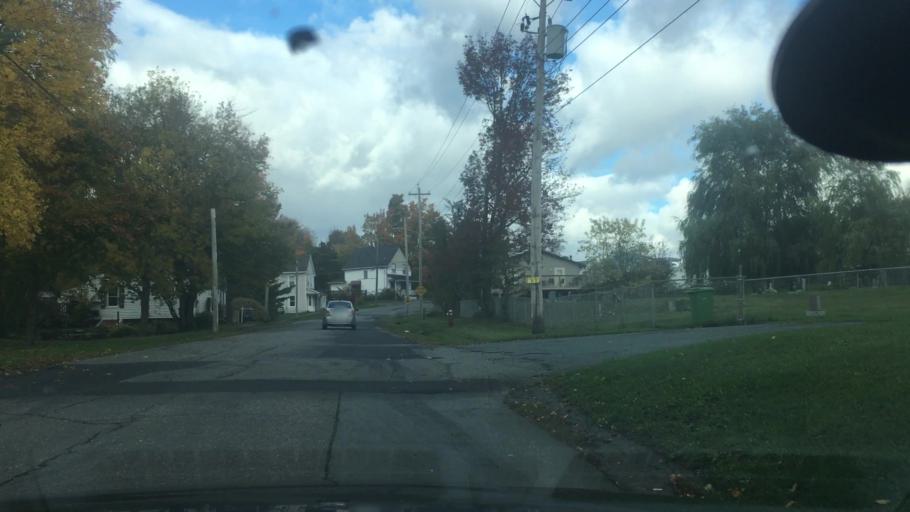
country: CA
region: Nova Scotia
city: Windsor
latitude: 44.9861
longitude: -64.1340
